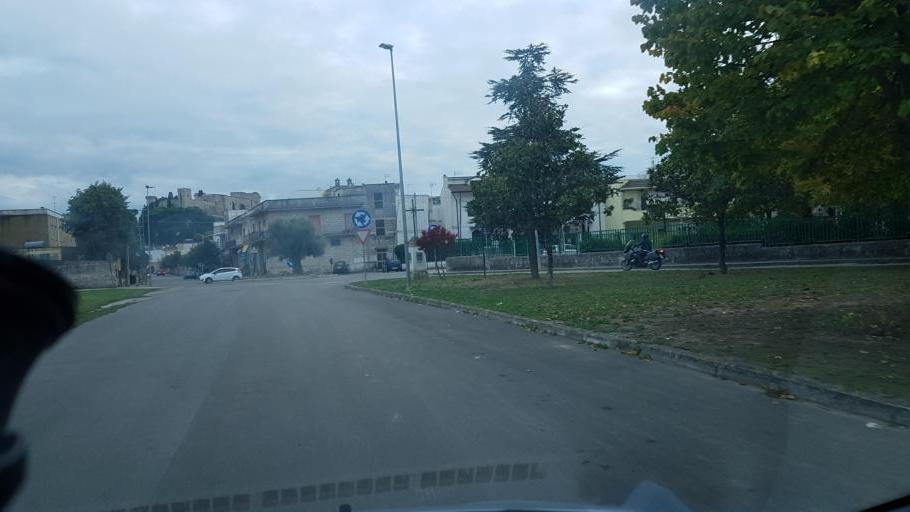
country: IT
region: Apulia
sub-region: Provincia di Brindisi
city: Oria
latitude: 40.5043
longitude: 17.6396
